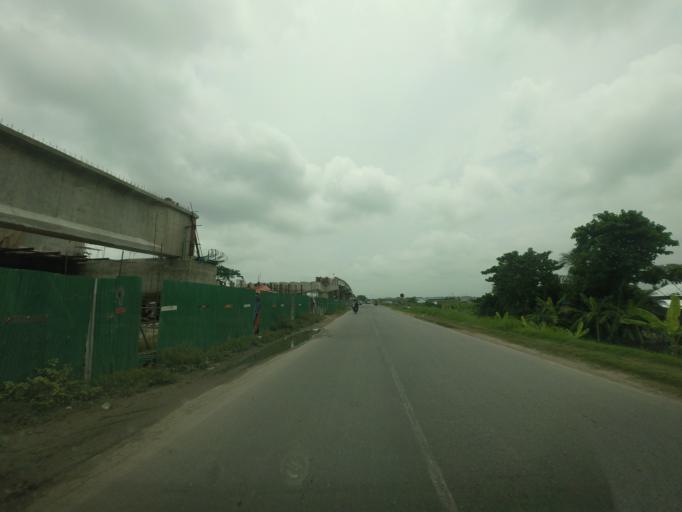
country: BD
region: Khulna
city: Kalia
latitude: 23.2154
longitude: 89.7141
